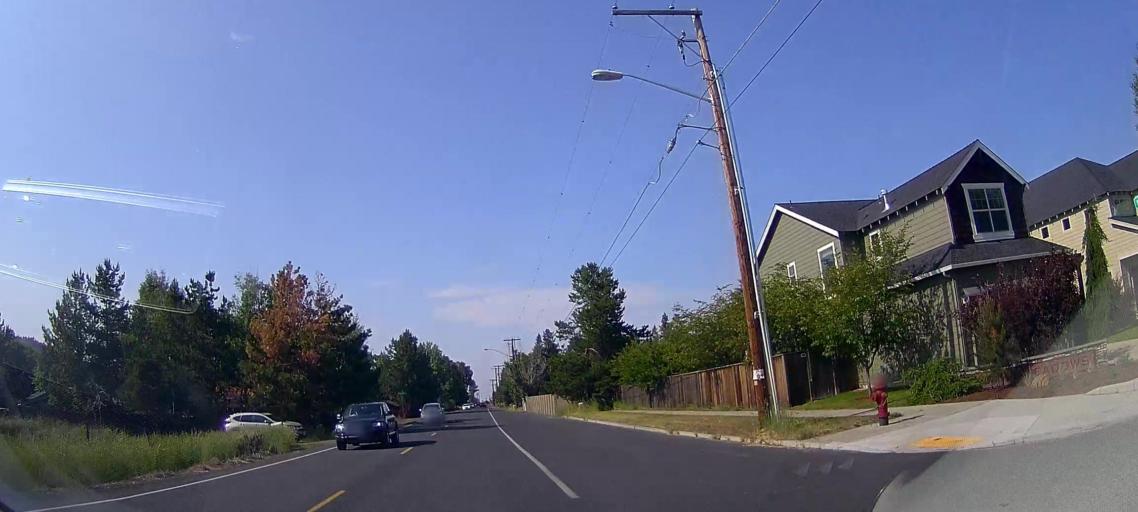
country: US
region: Oregon
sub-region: Deschutes County
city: Bend
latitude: 44.0485
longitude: -121.2686
